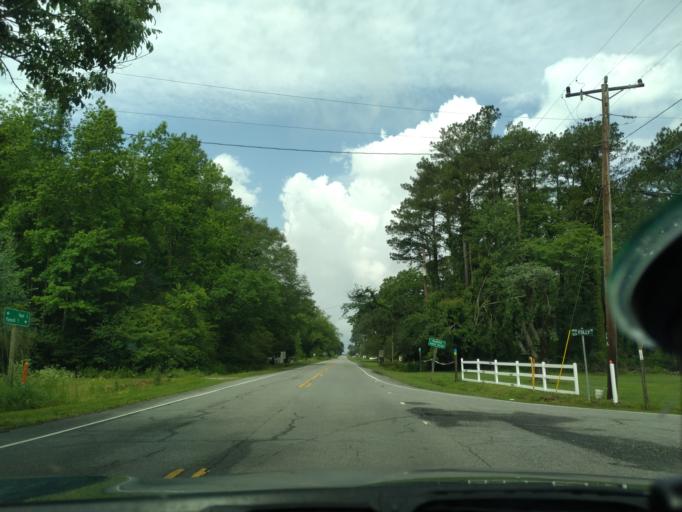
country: US
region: North Carolina
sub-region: Washington County
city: Plymouth
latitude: 35.8758
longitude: -76.6645
